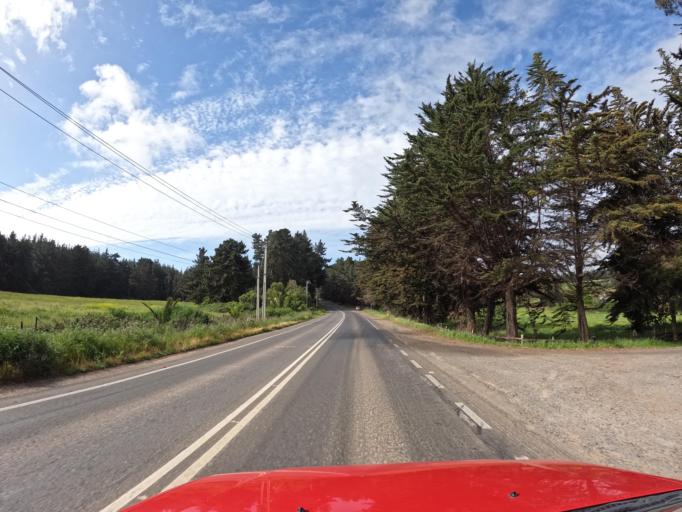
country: CL
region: O'Higgins
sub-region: Provincia de Colchagua
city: Santa Cruz
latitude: -34.3738
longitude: -71.9680
